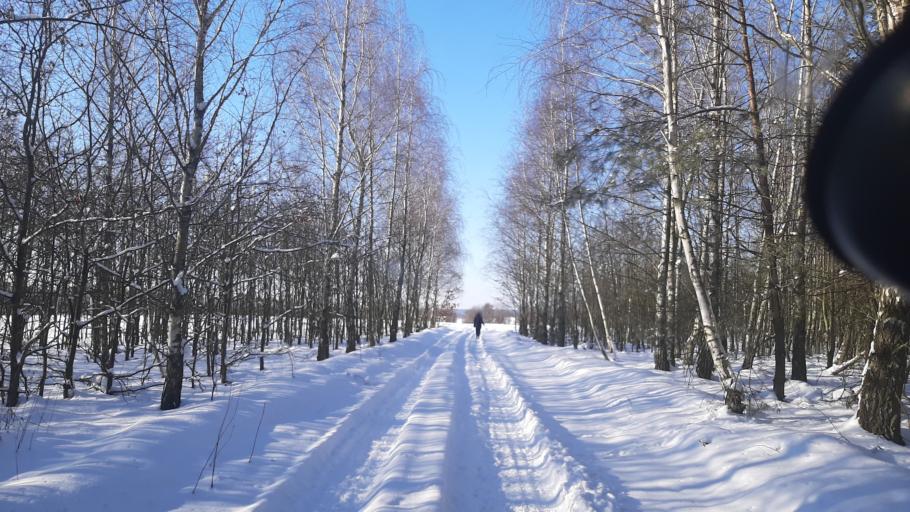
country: PL
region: Lublin Voivodeship
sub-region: Powiat lubelski
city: Jastkow
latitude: 51.3767
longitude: 22.4379
